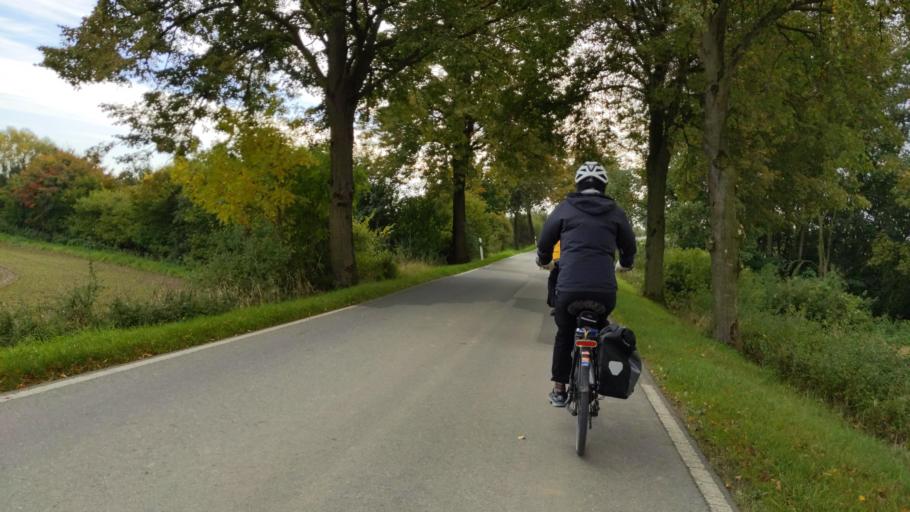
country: DE
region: Schleswig-Holstein
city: Rehhorst
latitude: 53.8854
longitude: 10.4755
